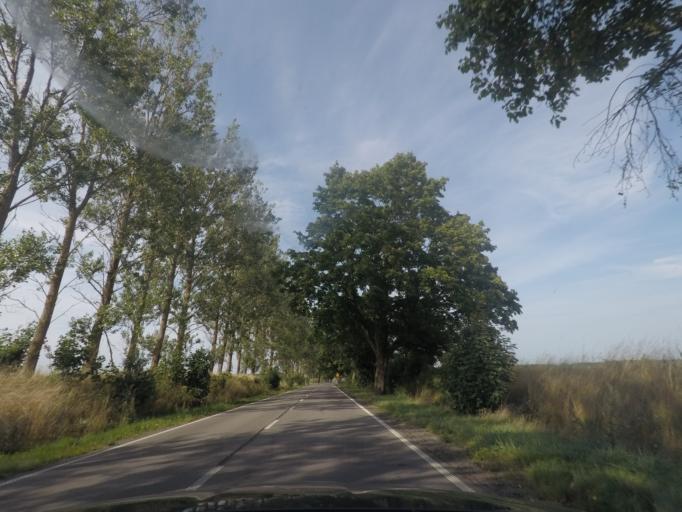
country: PL
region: Pomeranian Voivodeship
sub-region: Powiat leborski
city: Leba
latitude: 54.6483
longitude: 17.5538
